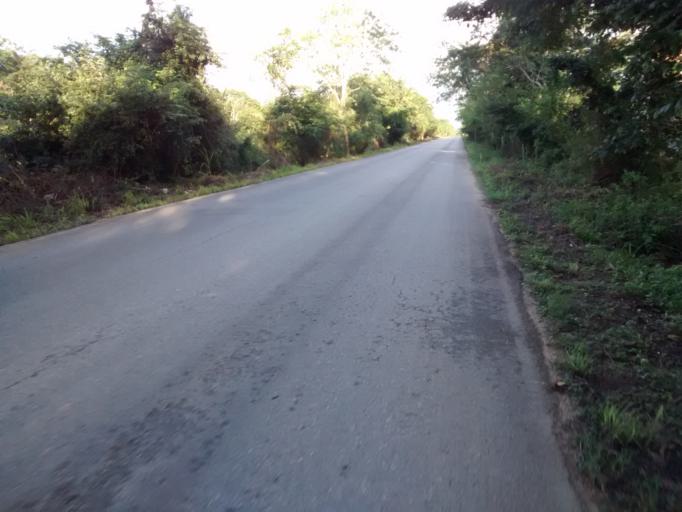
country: MX
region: Yucatan
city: Valladolid
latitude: 20.7311
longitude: -88.2126
